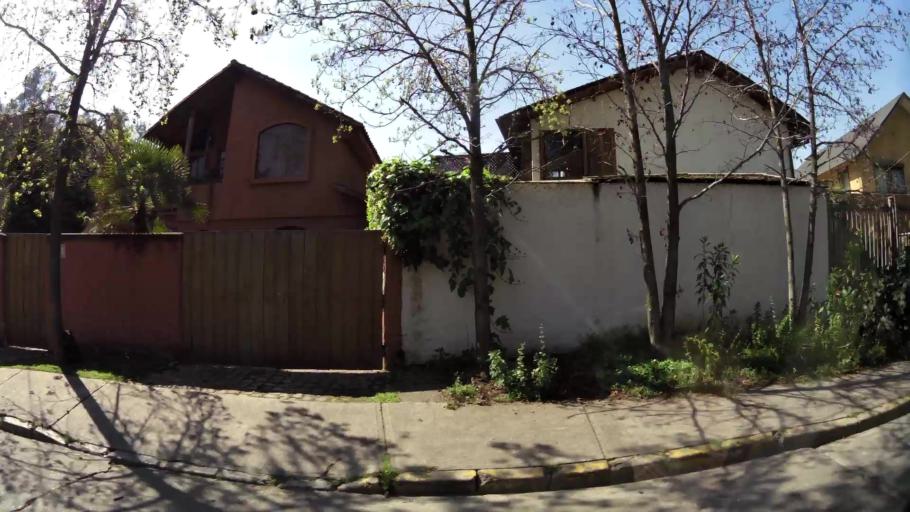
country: CL
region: Santiago Metropolitan
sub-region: Provincia de Santiago
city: Santiago
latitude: -33.4172
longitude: -70.6184
